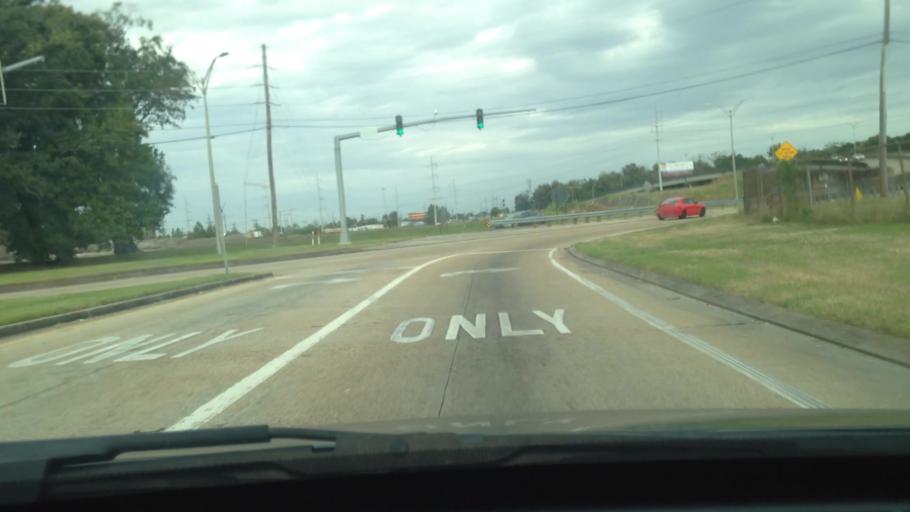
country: US
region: Louisiana
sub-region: Jefferson Parish
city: River Ridge
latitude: 29.9704
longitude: -90.2043
